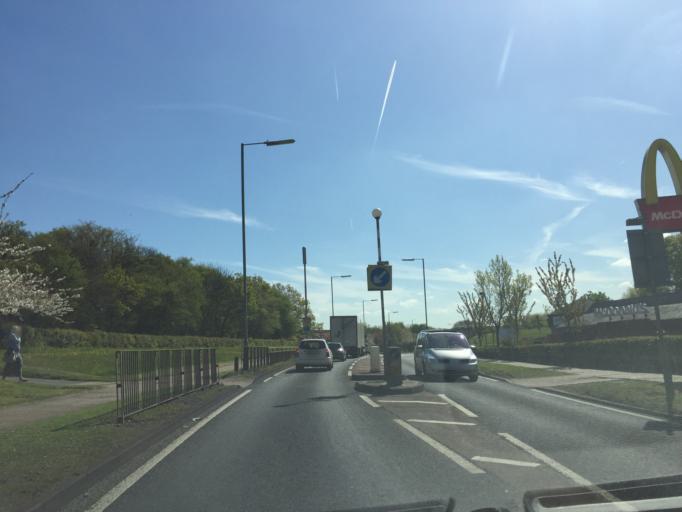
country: GB
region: England
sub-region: Essex
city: Harlow
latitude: 51.7540
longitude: 0.0926
